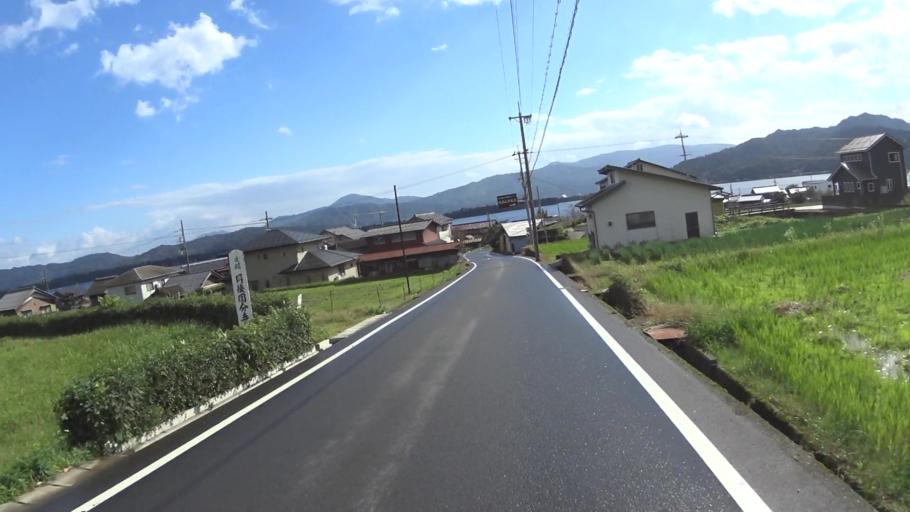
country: JP
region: Kyoto
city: Miyazu
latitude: 35.5787
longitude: 135.1790
